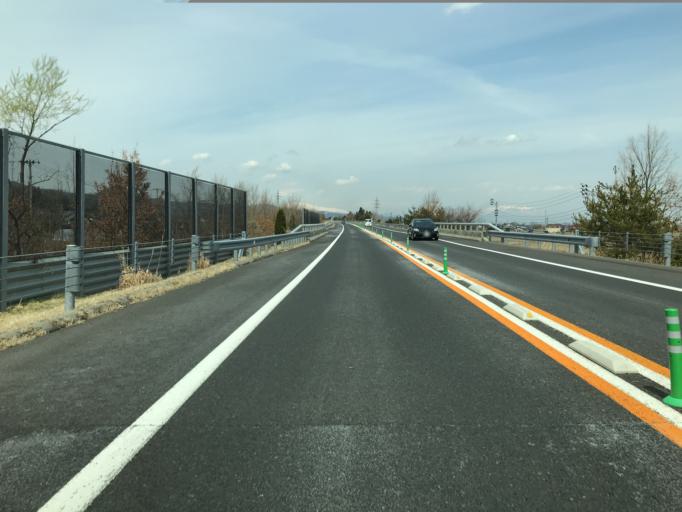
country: JP
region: Yamagata
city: Kaminoyama
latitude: 38.2076
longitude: 140.2937
